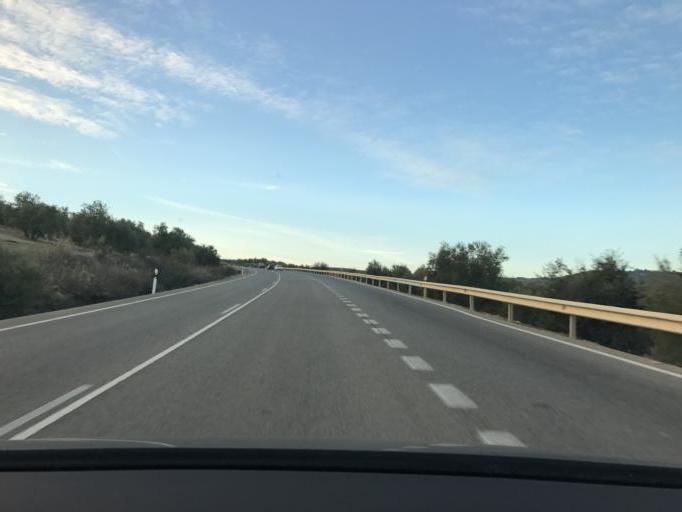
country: ES
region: Andalusia
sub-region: Provincia de Jaen
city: Ubeda
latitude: 37.9689
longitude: -3.3670
